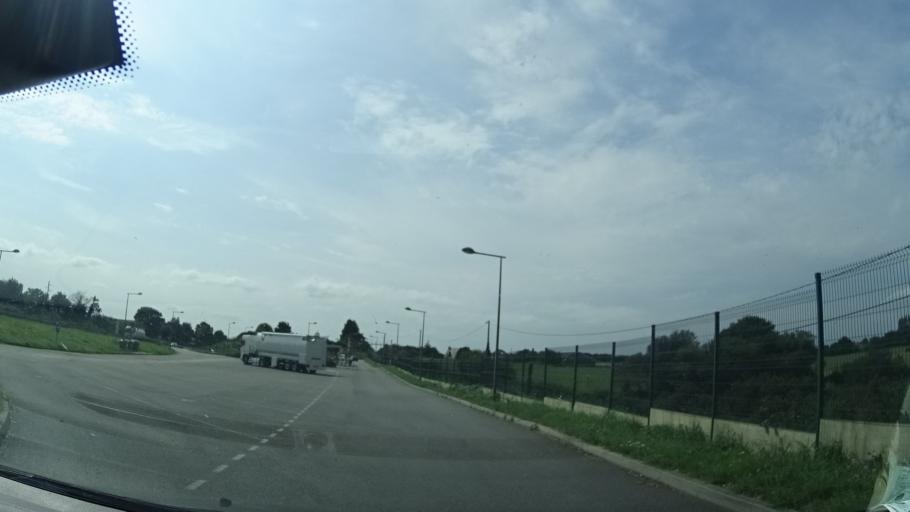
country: FR
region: Brittany
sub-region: Departement du Finistere
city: Bodilis
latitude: 48.5038
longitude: -4.1490
